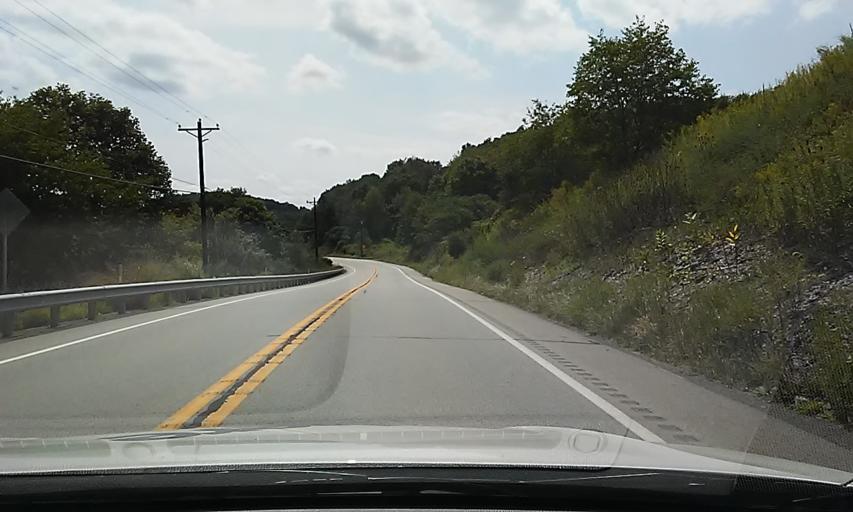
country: US
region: Pennsylvania
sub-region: Indiana County
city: Clymer
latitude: 40.8084
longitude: -79.0533
